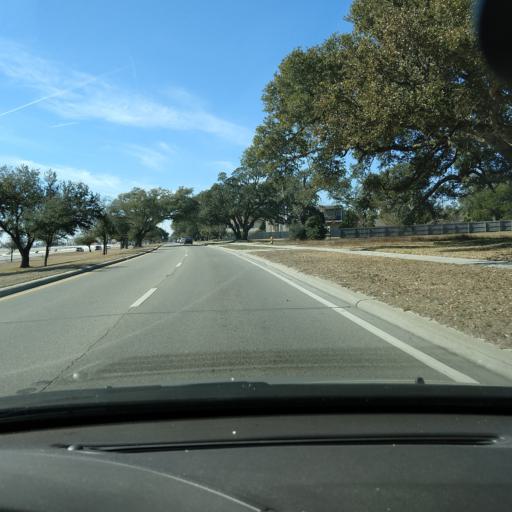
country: US
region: Mississippi
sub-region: Harrison County
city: Gulfport
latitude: 30.3715
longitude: -89.0755
